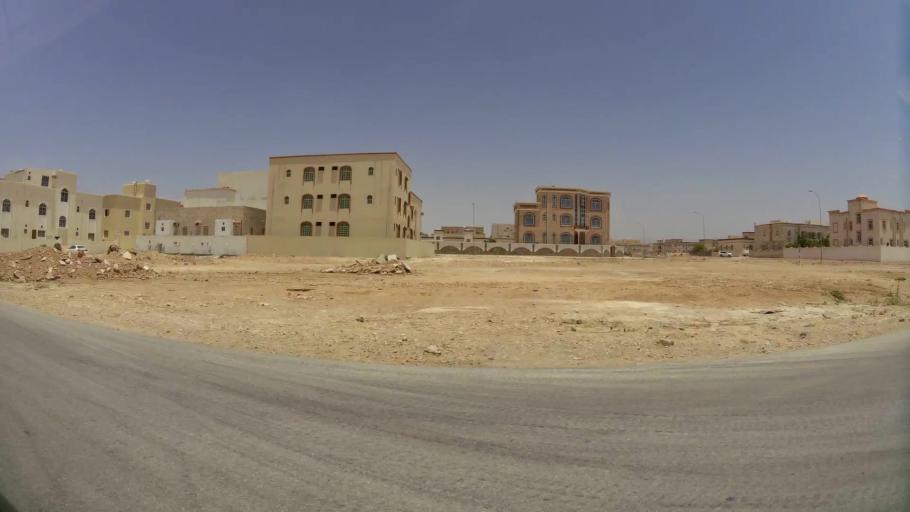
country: OM
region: Zufar
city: Salalah
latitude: 17.0943
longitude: 54.1595
